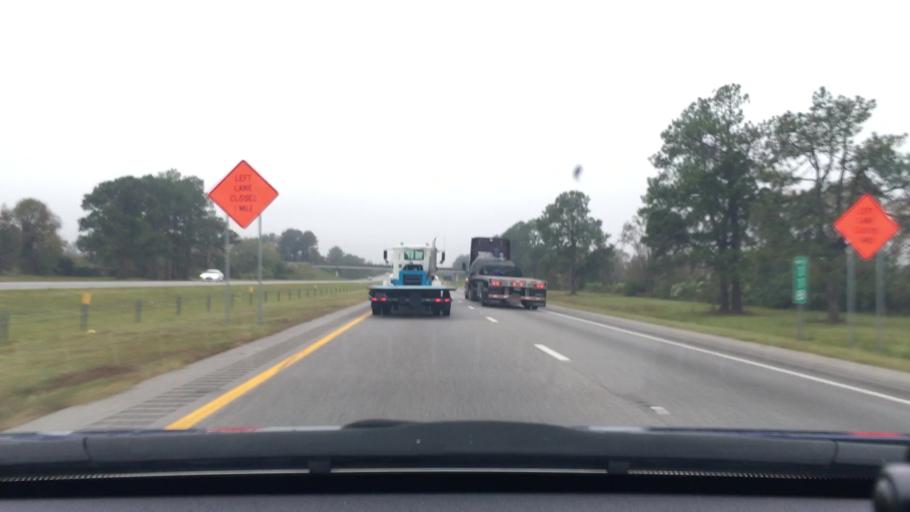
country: US
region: South Carolina
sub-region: Lee County
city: Bishopville
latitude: 34.1896
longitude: -80.2462
